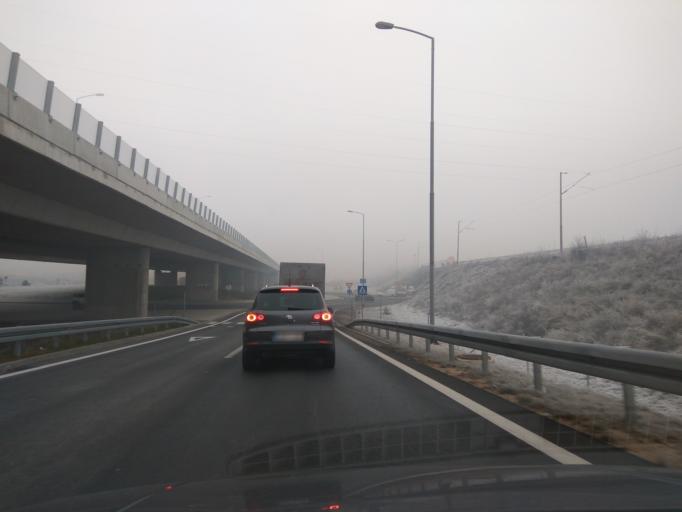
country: BA
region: Federation of Bosnia and Herzegovina
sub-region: Kanton Sarajevo
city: Sarajevo
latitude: 43.8513
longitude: 18.3252
